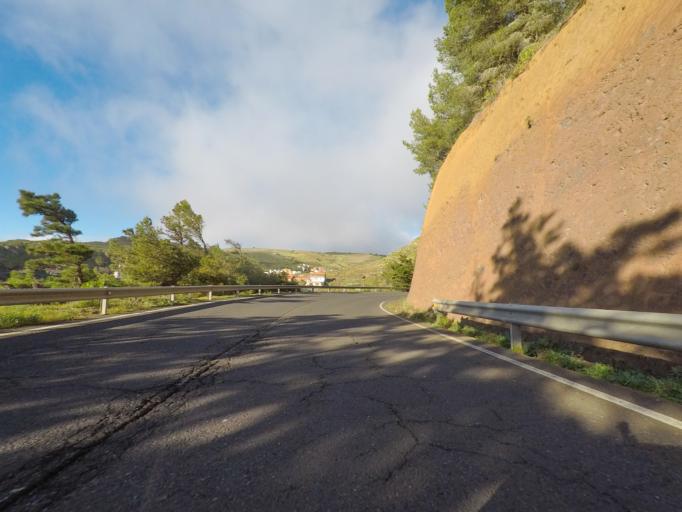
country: ES
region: Canary Islands
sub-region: Provincia de Santa Cruz de Tenerife
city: Vallehermosa
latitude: 28.1290
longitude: -17.3213
